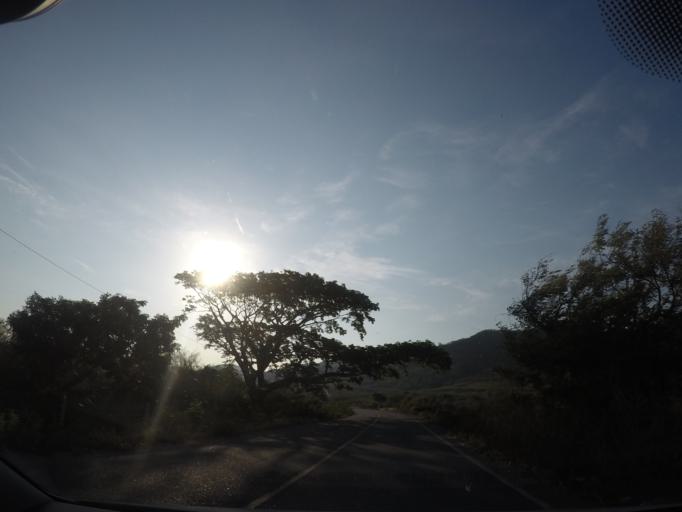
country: MX
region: Oaxaca
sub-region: Santo Domingo Tehuantepec
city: La Noria
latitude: 16.2307
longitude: -95.1794
